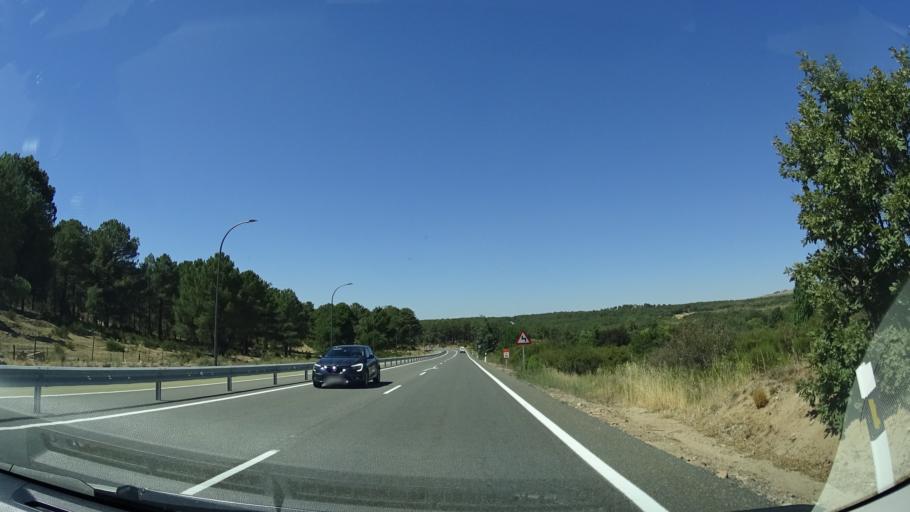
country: ES
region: Castille and Leon
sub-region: Provincia de Avila
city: Las Navas del Marques
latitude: 40.5951
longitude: -4.3551
